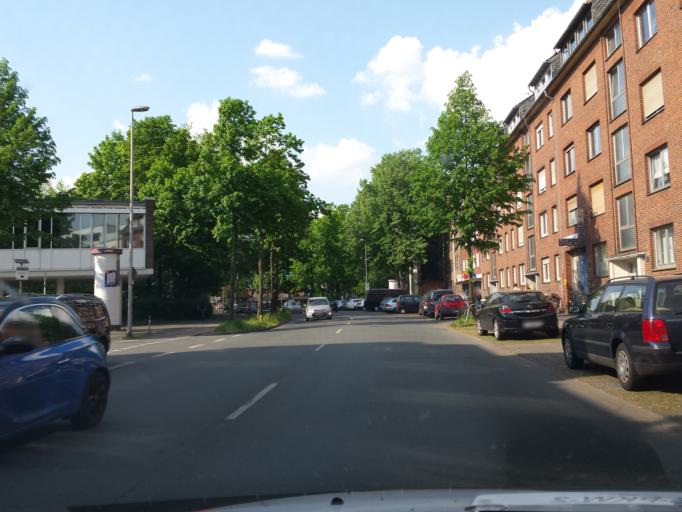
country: DE
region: North Rhine-Westphalia
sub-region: Regierungsbezirk Munster
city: Muenster
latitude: 51.9498
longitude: 7.6319
